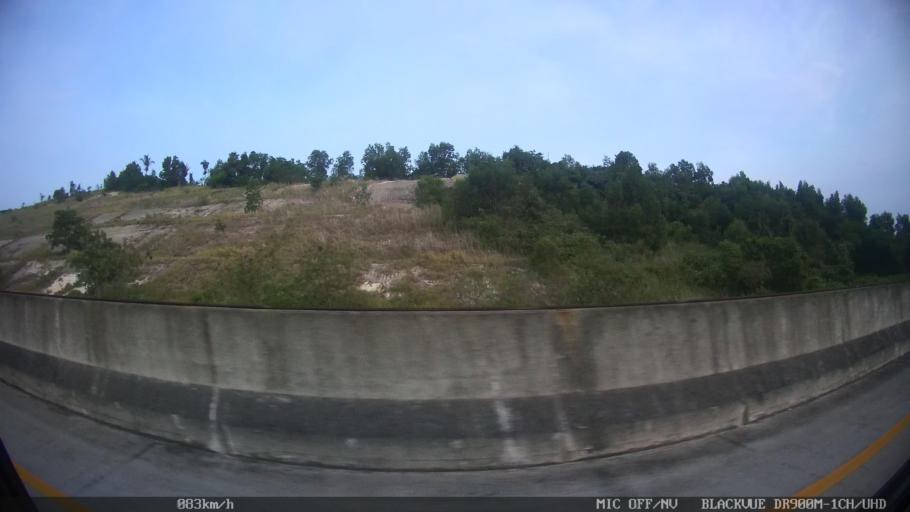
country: ID
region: Lampung
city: Penengahan
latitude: -5.8284
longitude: 105.7331
